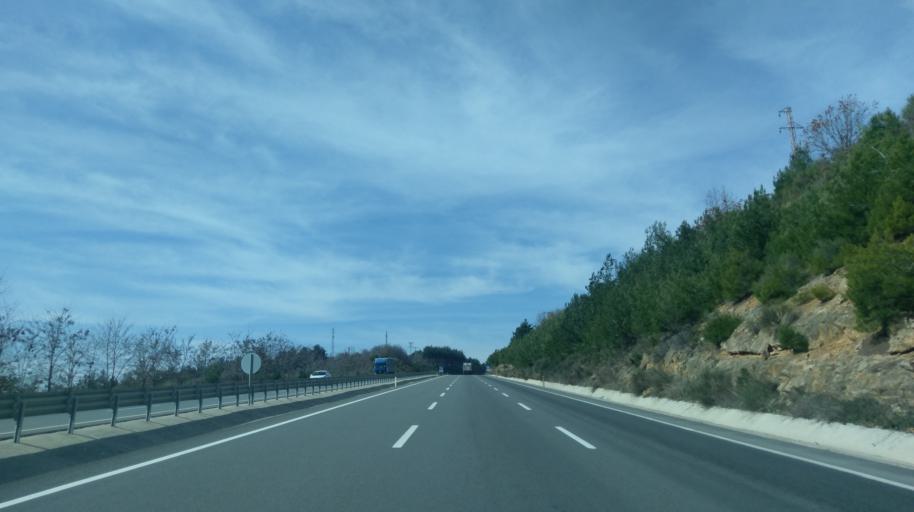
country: TR
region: Canakkale
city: Evrese
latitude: 40.7080
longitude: 26.7753
